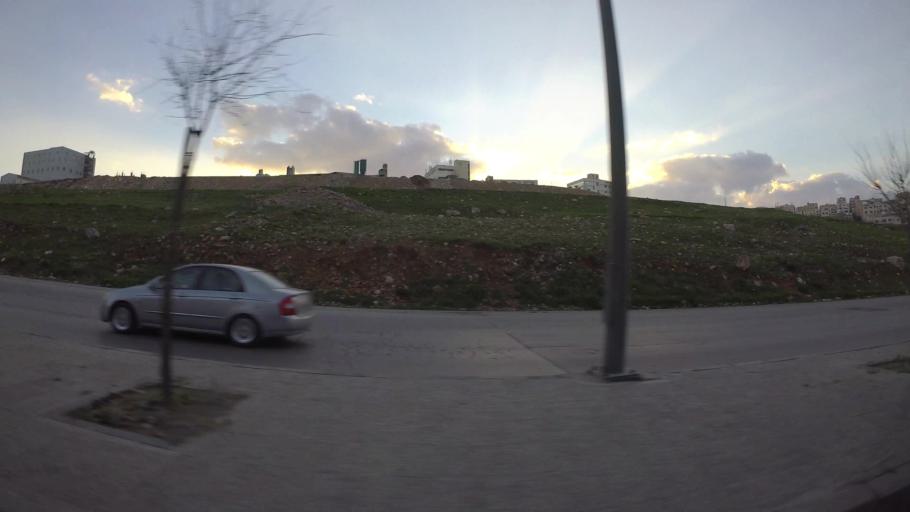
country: JO
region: Amman
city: Al Bunayyat ash Shamaliyah
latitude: 31.9238
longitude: 35.9112
